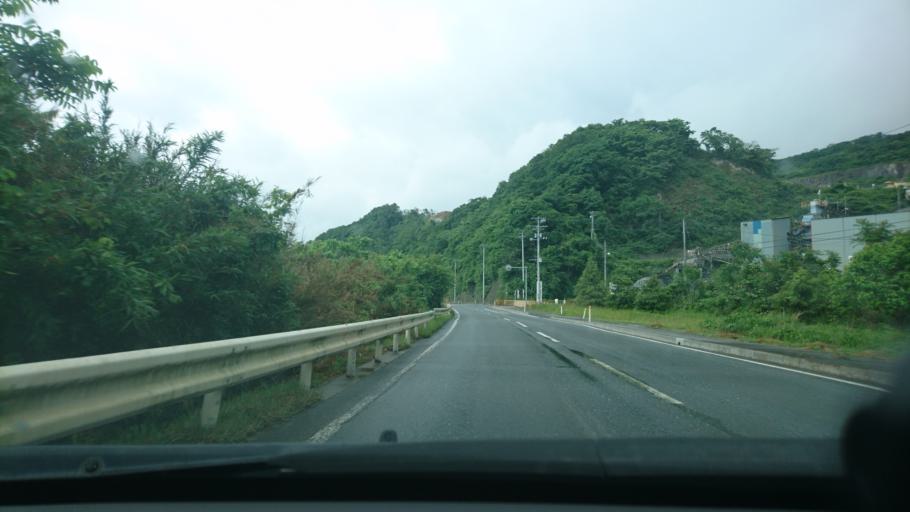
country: JP
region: Miyagi
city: Ishinomaki
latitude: 38.5811
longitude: 141.3029
